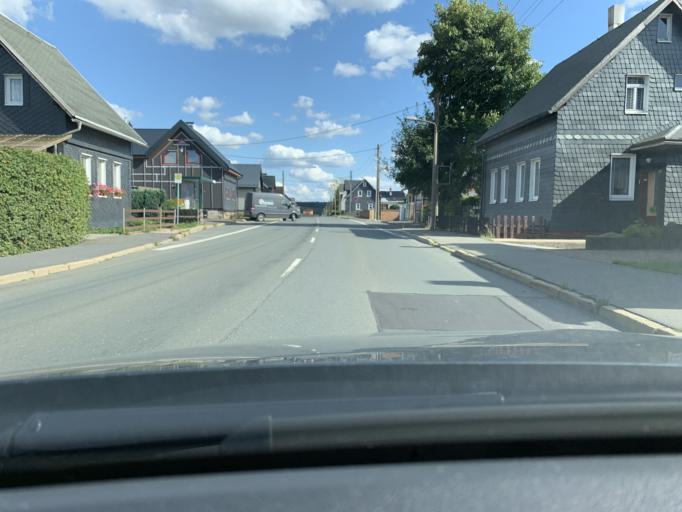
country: DE
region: Thuringia
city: Lauscha
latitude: 50.4968
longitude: 11.1544
